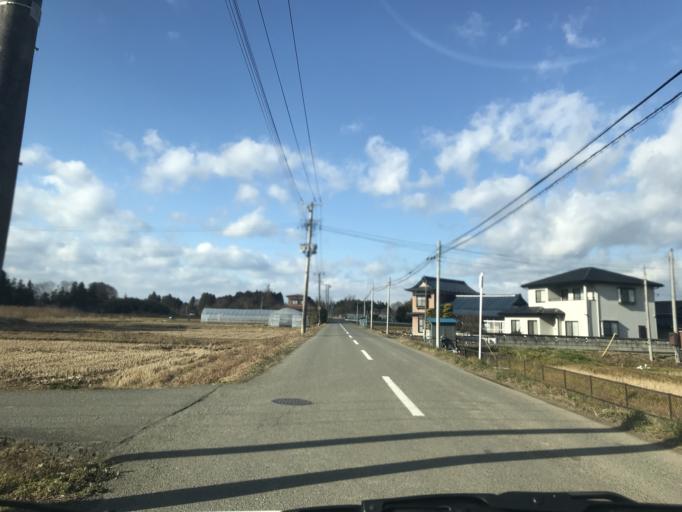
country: JP
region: Miyagi
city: Kogota
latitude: 38.7384
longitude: 141.0587
